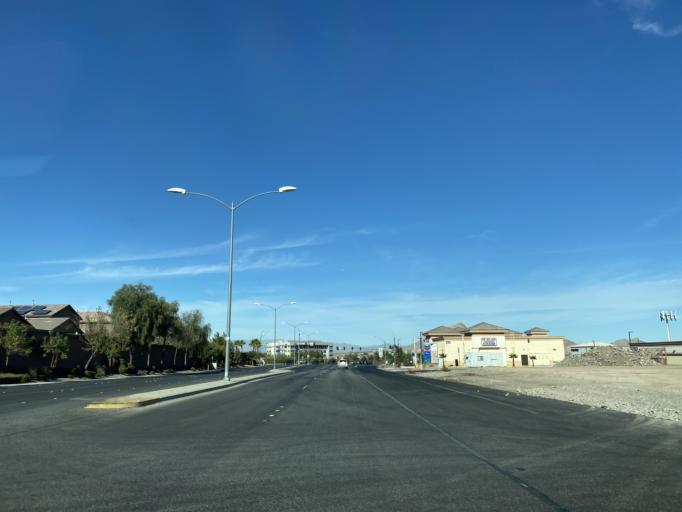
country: US
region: Nevada
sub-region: Clark County
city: Henderson
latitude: 36.0690
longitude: -115.0287
